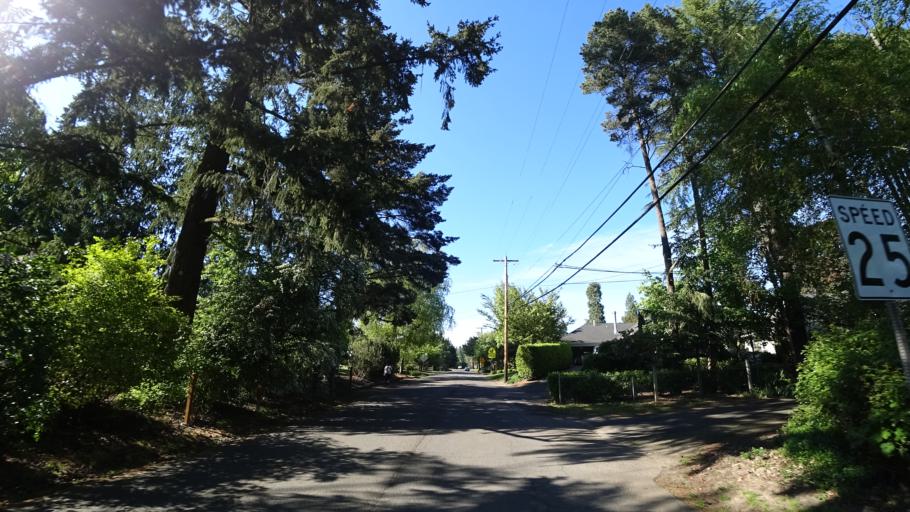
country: US
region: Oregon
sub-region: Washington County
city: West Slope
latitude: 45.4912
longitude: -122.7575
